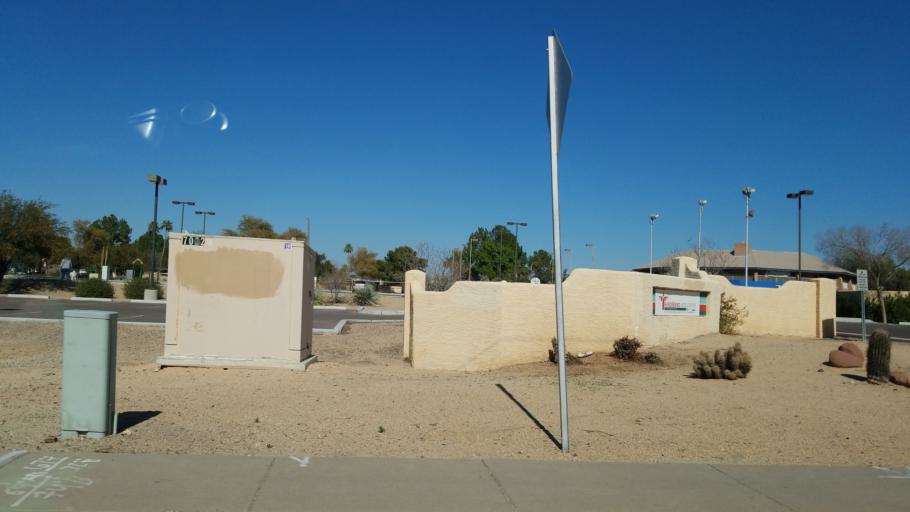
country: US
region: Arizona
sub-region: Maricopa County
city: Paradise Valley
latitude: 33.6475
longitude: -112.0603
